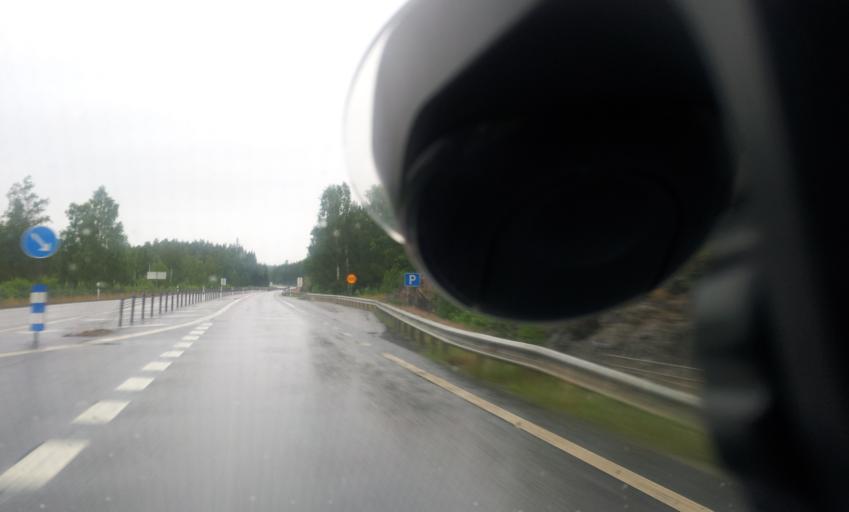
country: SE
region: OEstergoetland
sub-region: Valdemarsviks Kommun
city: Valdemarsvik
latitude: 58.1767
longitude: 16.5364
